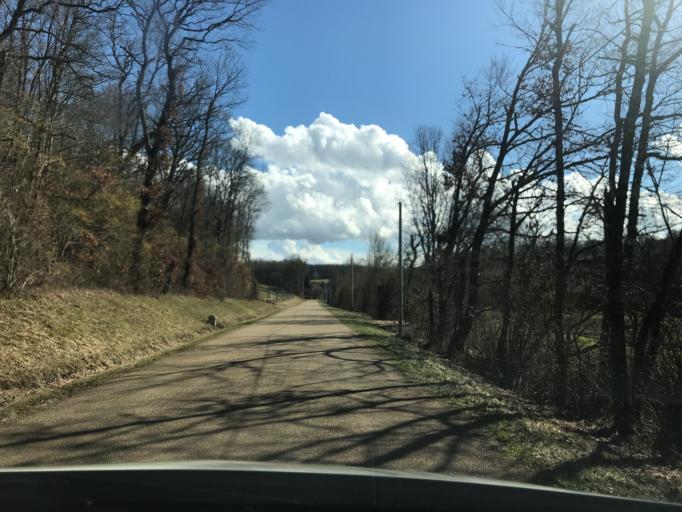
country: FR
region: Bourgogne
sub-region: Departement de l'Yonne
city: Fontenailles
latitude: 47.5542
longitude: 3.3423
